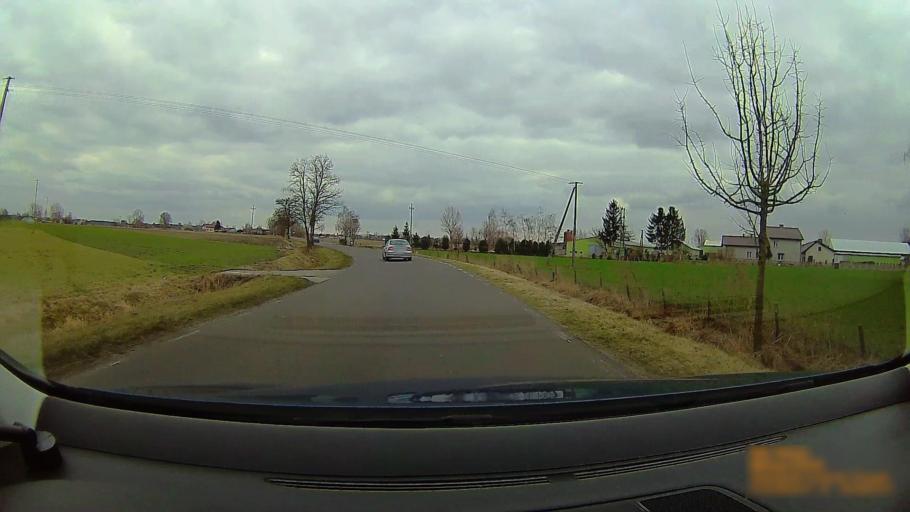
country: PL
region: Greater Poland Voivodeship
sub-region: Powiat koninski
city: Rzgow Pierwszy
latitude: 52.1136
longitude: 18.0728
